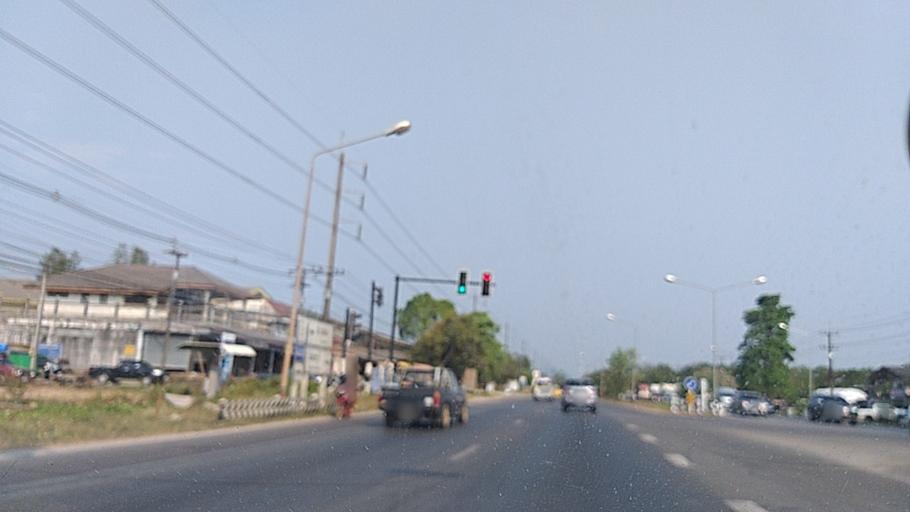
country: TH
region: Chanthaburi
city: Na Yai Am
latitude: 12.7332
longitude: 101.9055
